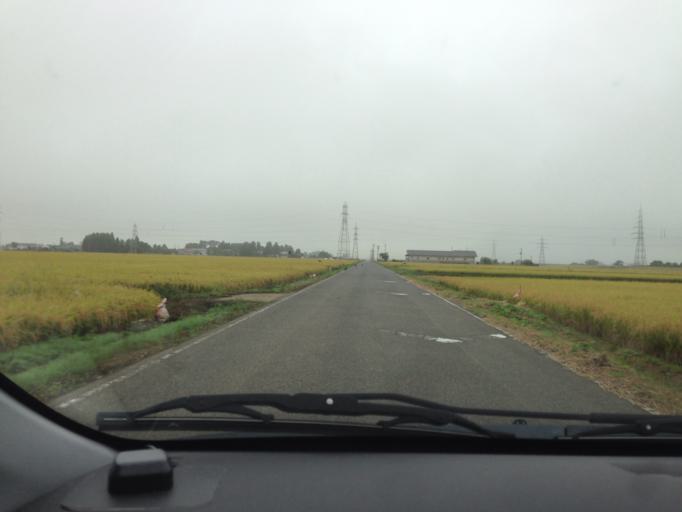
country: JP
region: Fukushima
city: Kitakata
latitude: 37.5801
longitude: 139.8659
